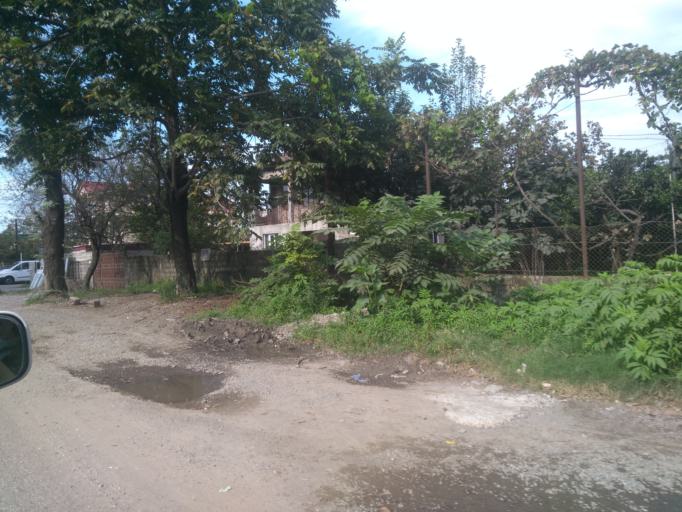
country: GE
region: Ajaria
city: Batumi
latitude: 41.6159
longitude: 41.6204
